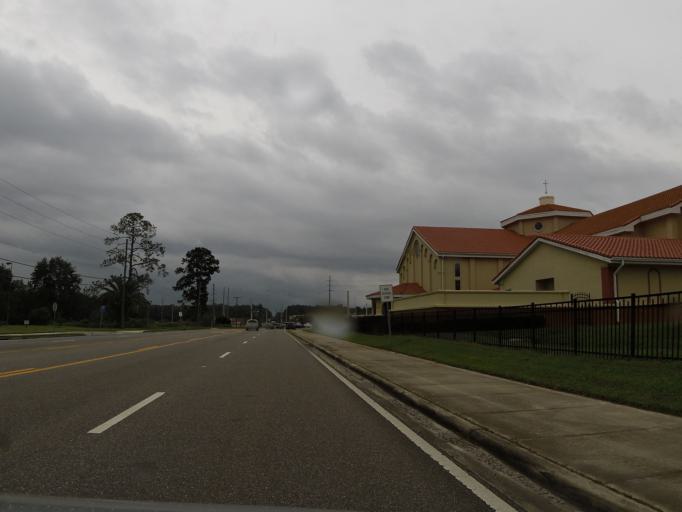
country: US
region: Florida
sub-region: Clay County
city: Lakeside
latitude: 30.1146
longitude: -81.8153
